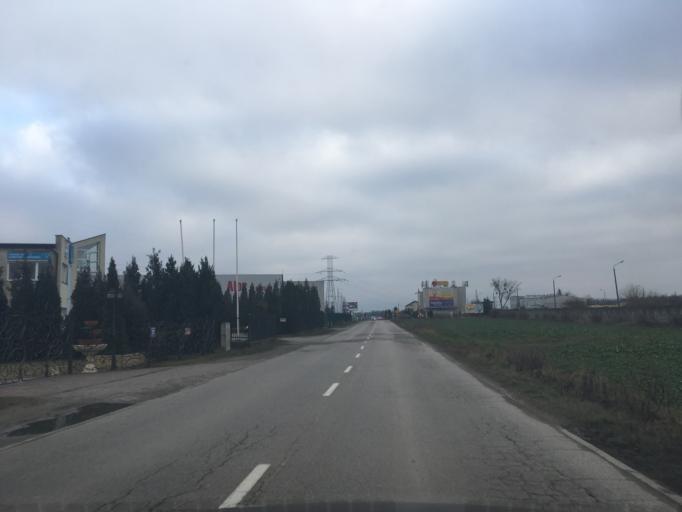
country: PL
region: Masovian Voivodeship
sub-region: Powiat piaseczynski
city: Lesznowola
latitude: 52.0840
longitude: 20.9687
